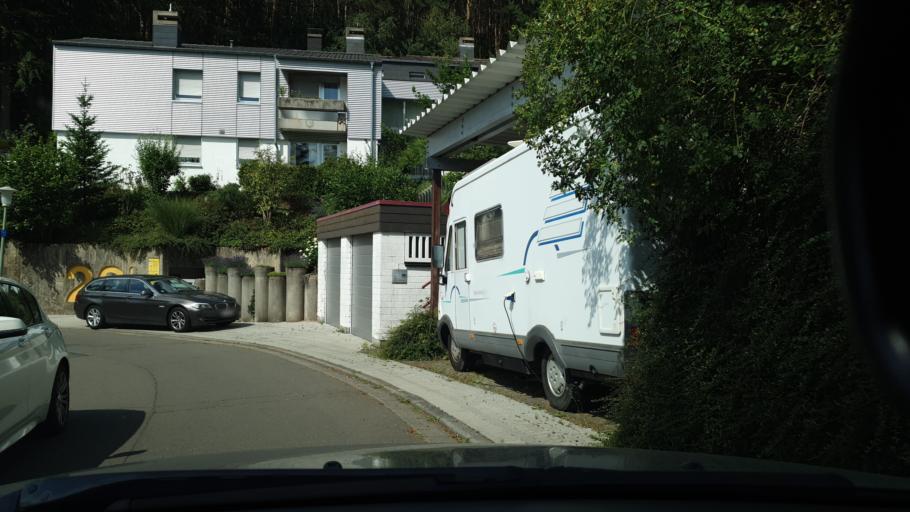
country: DE
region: Rheinland-Pfalz
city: Otterberg
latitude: 49.4803
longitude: 7.7732
